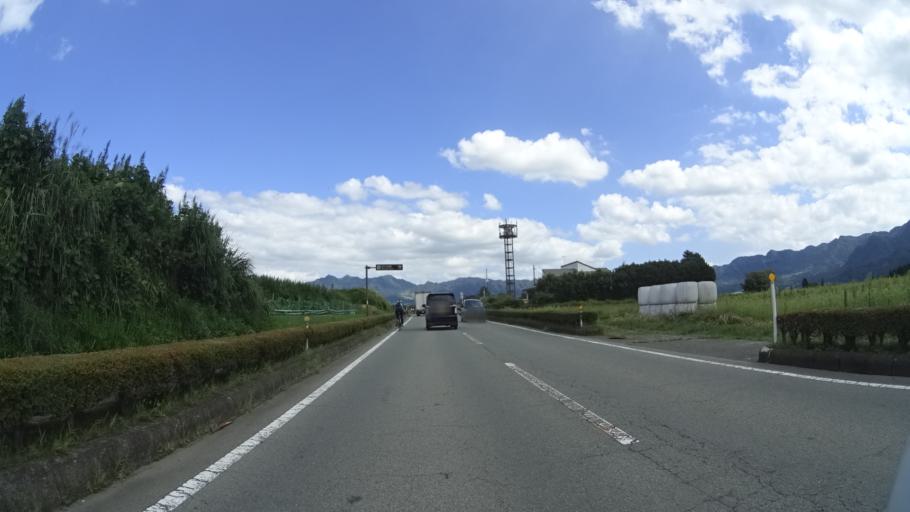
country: JP
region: Kumamoto
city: Aso
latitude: 32.8302
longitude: 131.0880
